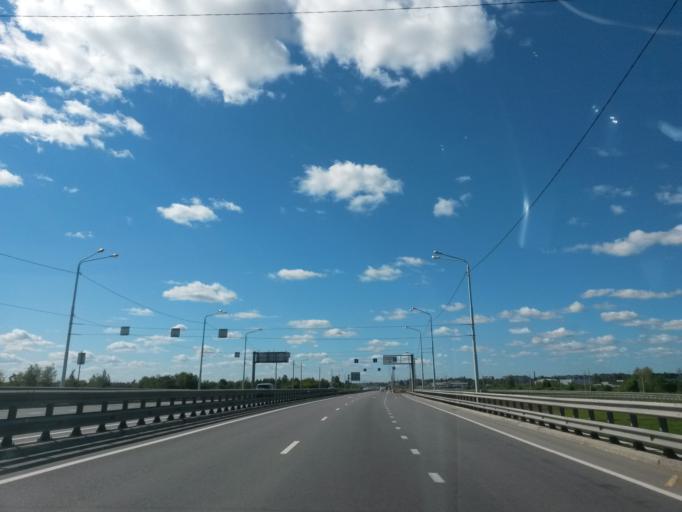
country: RU
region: Jaroslavl
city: Yaroslavl
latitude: 57.6675
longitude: 39.8188
